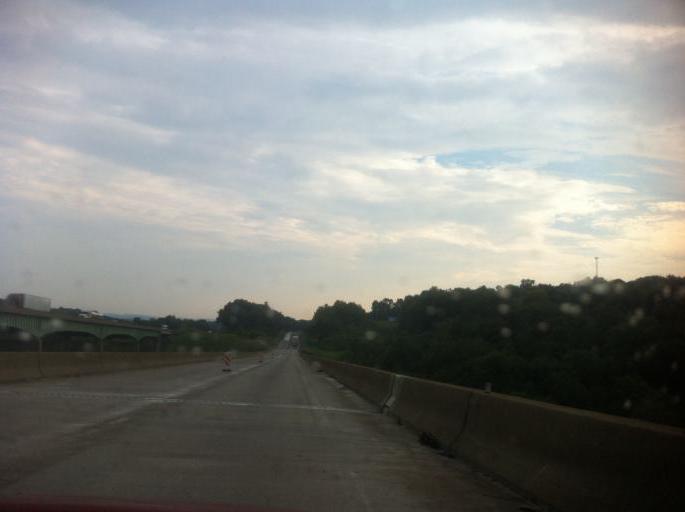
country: US
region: Pennsylvania
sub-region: Clarion County
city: Knox
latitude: 41.1918
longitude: -79.5136
